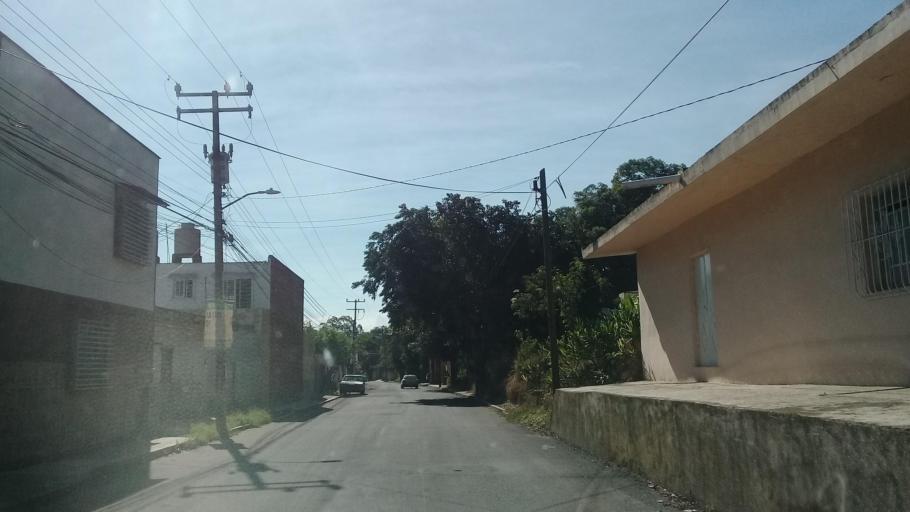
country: MX
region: Veracruz
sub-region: Tlalnelhuayocan
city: Guadalupe Victoria
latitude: 19.5506
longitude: -96.9532
